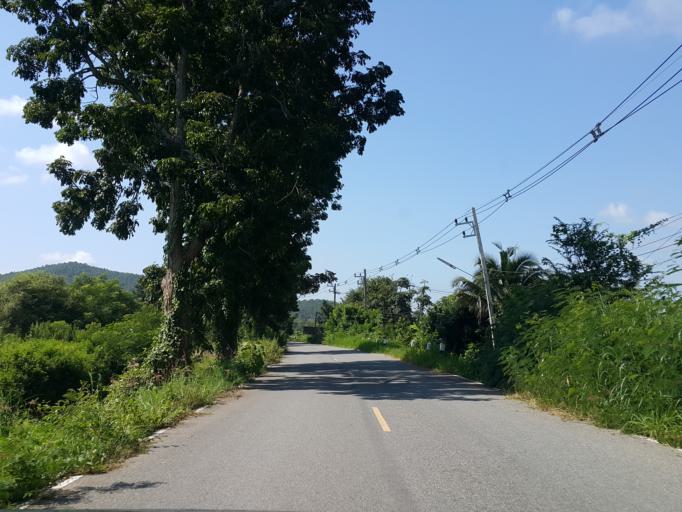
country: TH
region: Chiang Mai
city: Mae On
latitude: 18.7884
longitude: 99.1836
